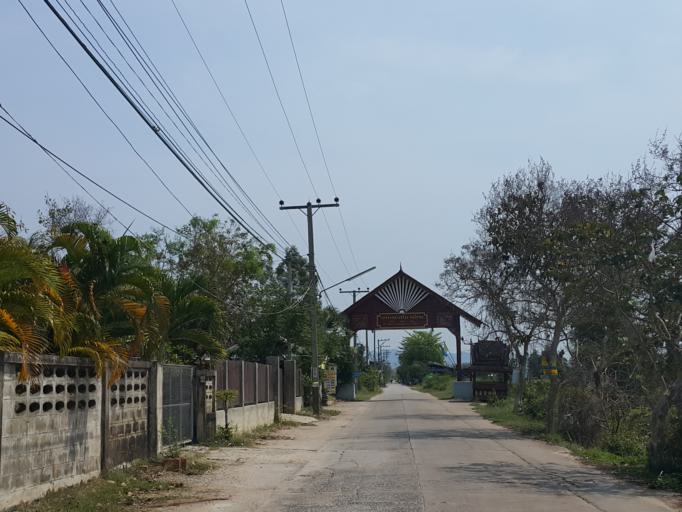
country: TH
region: Lampang
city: Lampang
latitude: 18.3029
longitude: 99.4309
